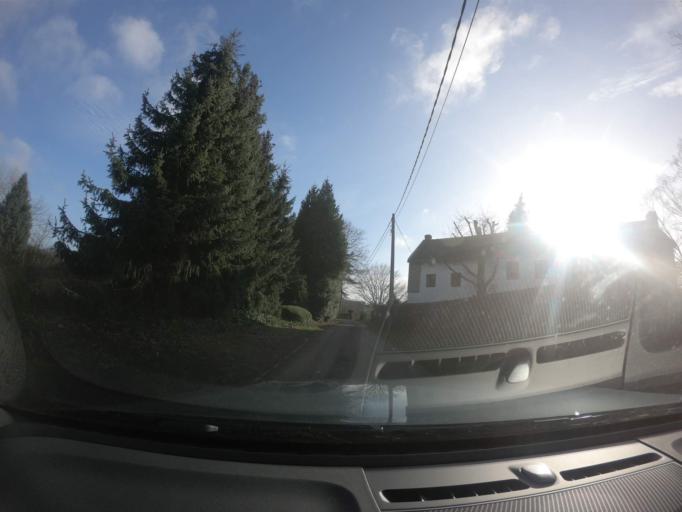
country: BE
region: Wallonia
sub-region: Province de Liege
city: Dison
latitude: 50.6283
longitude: 5.8325
